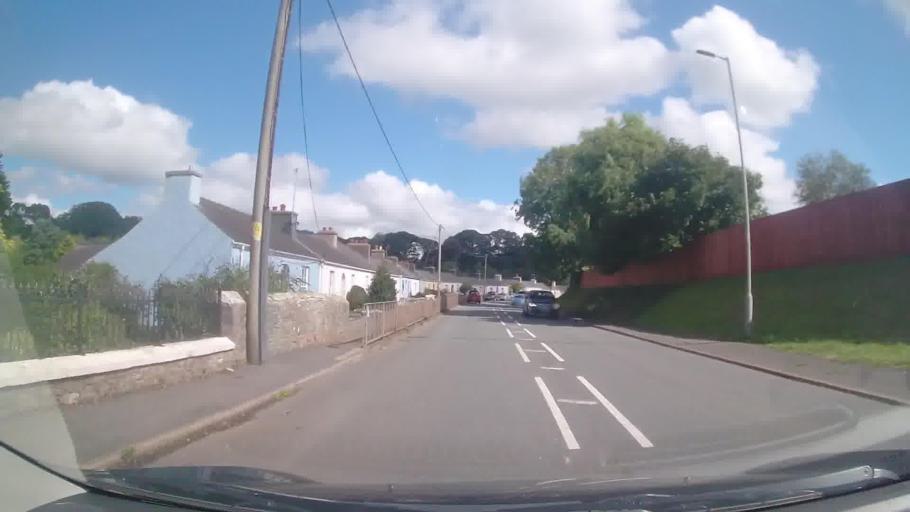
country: GB
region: Wales
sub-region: Pembrokeshire
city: Pembroke
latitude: 51.6766
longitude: -4.9020
